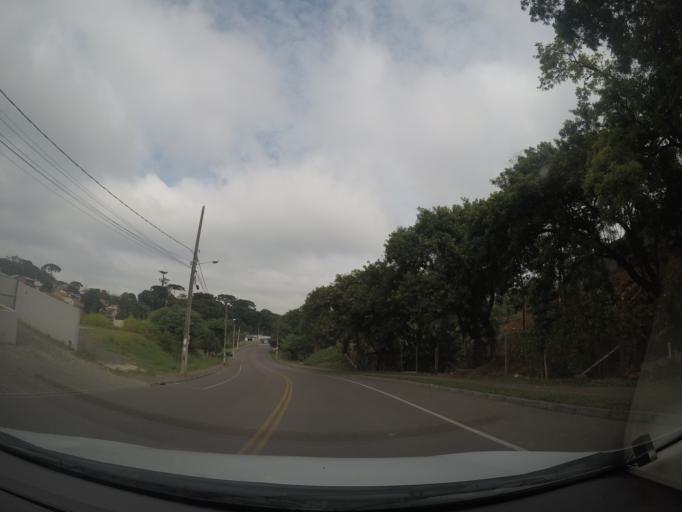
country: BR
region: Parana
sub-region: Colombo
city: Colombo
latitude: -25.3452
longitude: -49.2228
